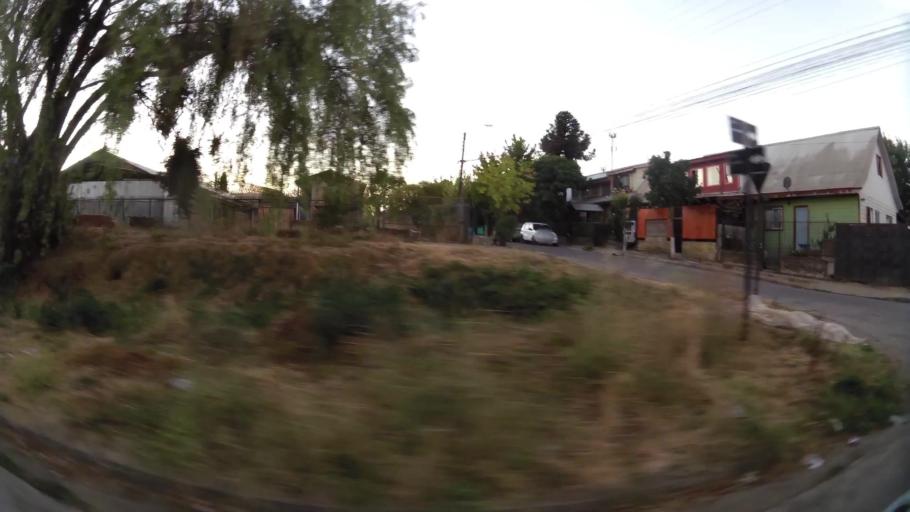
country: CL
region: Maule
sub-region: Provincia de Talca
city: Talca
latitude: -35.4490
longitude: -71.6277
